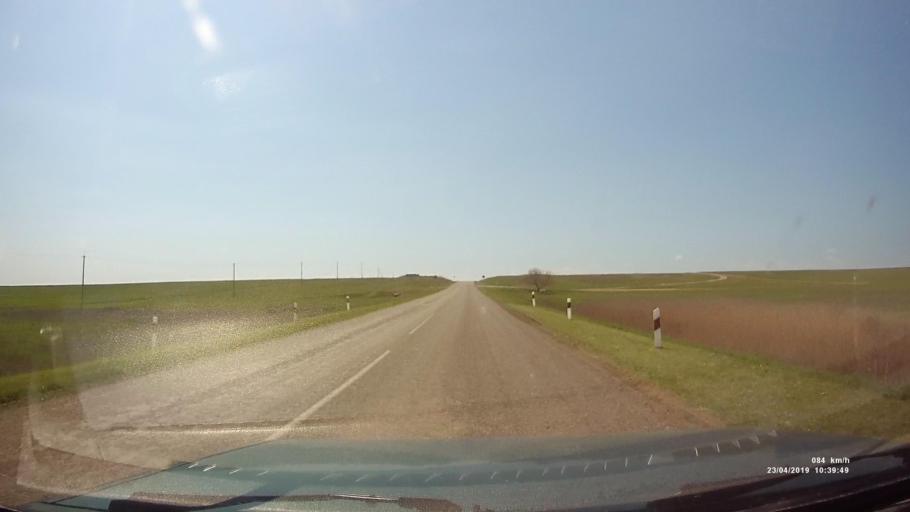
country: RU
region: Kalmykiya
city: Yashalta
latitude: 46.5143
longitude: 42.6386
